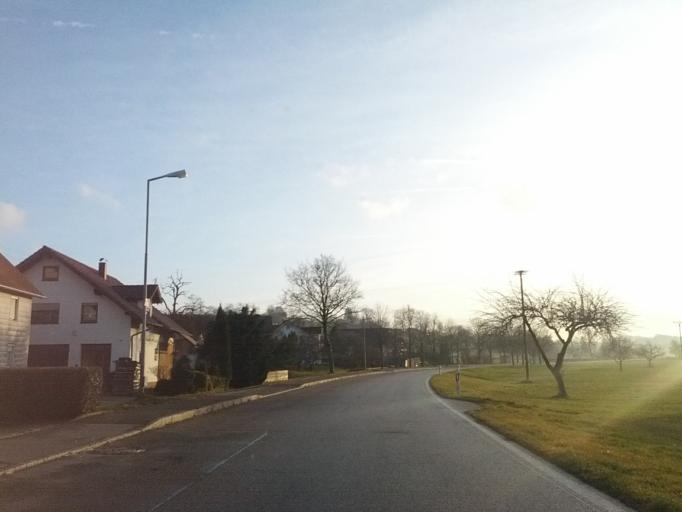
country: DE
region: Baden-Wuerttemberg
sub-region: Tuebingen Region
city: Erlenmoos
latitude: 48.0468
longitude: 9.9666
